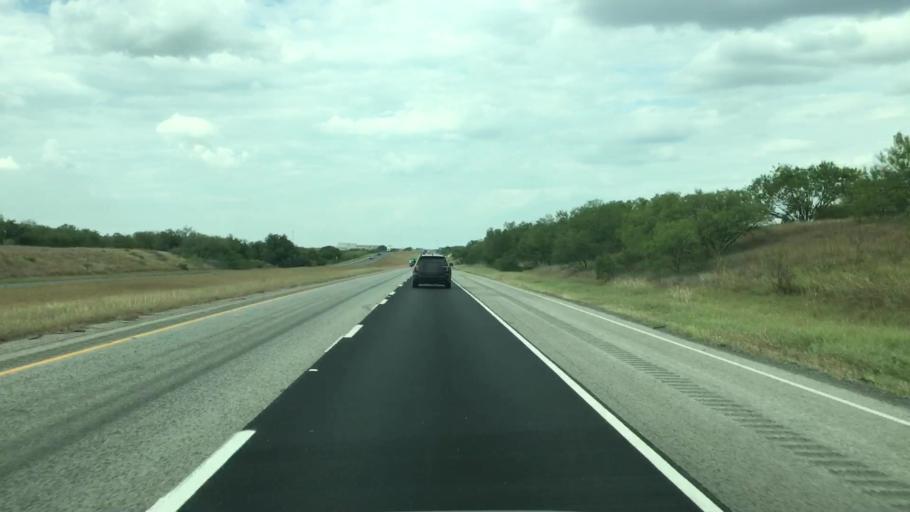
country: US
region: Texas
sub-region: Atascosa County
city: Pleasanton
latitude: 29.0798
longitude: -98.4328
